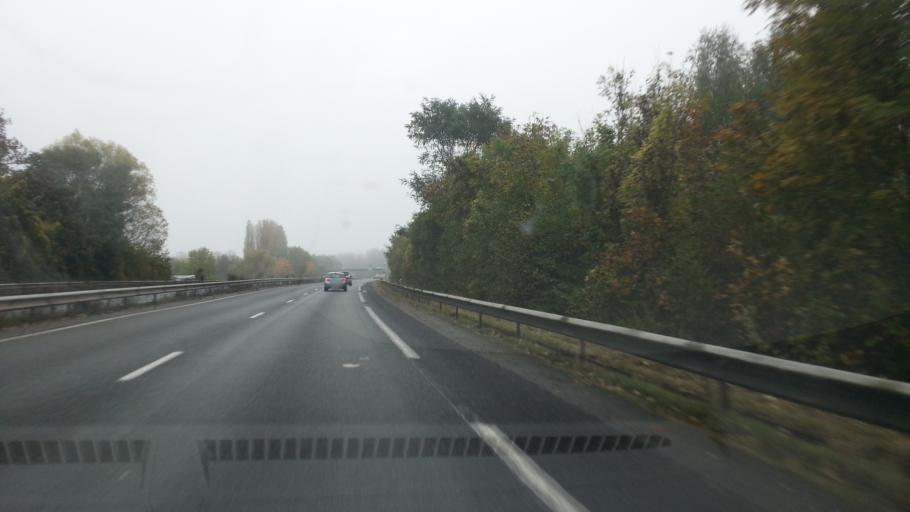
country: FR
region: Picardie
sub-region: Departement de l'Oise
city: Fitz-James
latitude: 49.3857
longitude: 2.4289
